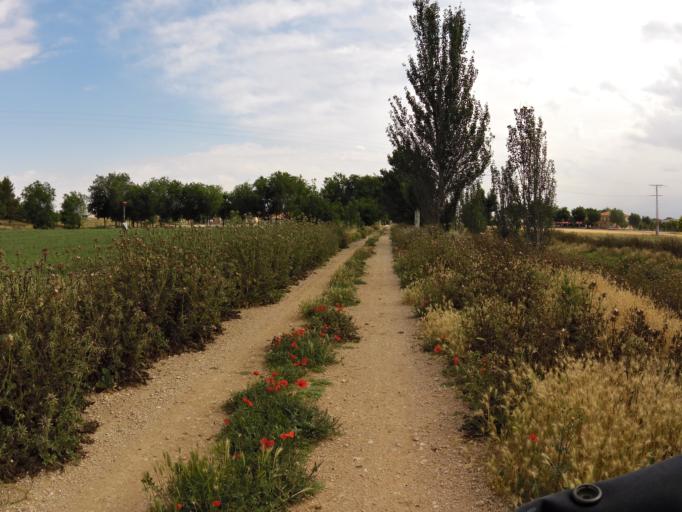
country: ES
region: Castille-La Mancha
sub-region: Provincia de Albacete
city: Valdeganga
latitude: 39.0652
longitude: -1.7460
